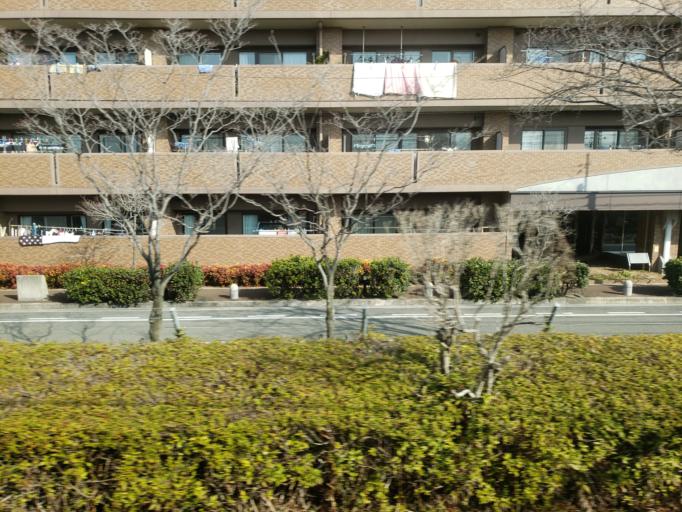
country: JP
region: Hyogo
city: Amagasaki
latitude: 34.7349
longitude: 135.4167
